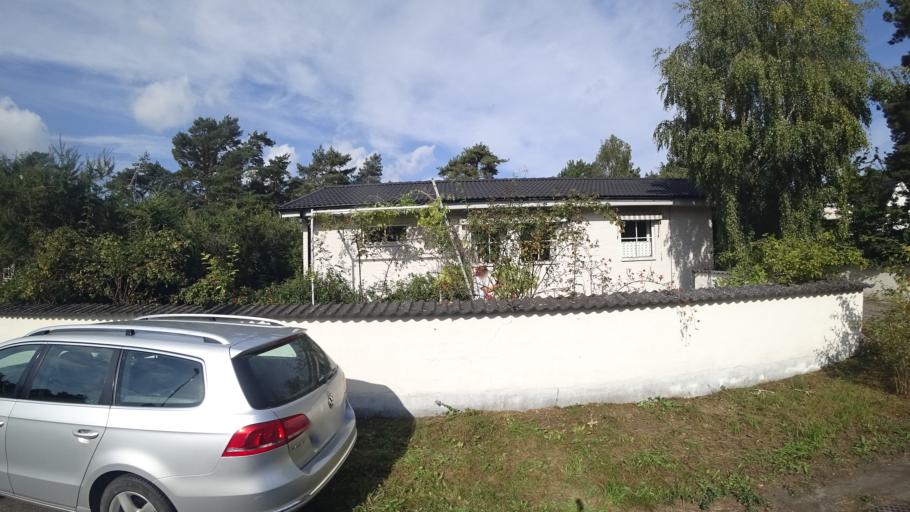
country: SE
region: Skane
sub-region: Kristianstads Kommun
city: Ahus
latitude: 55.9119
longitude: 14.2858
